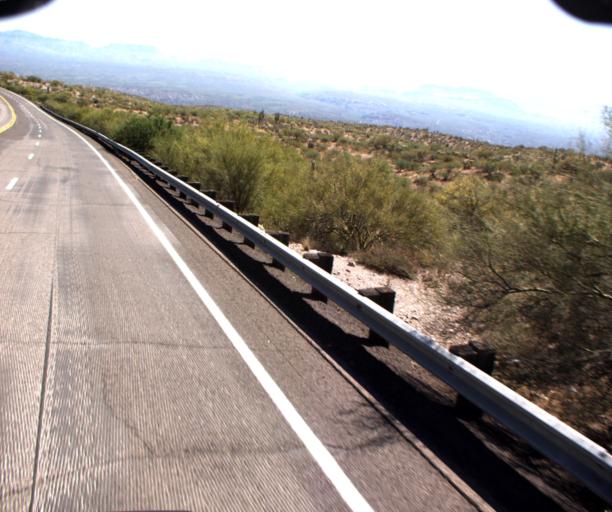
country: US
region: Arizona
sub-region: Pinal County
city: Mammoth
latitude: 32.6762
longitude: -110.6578
